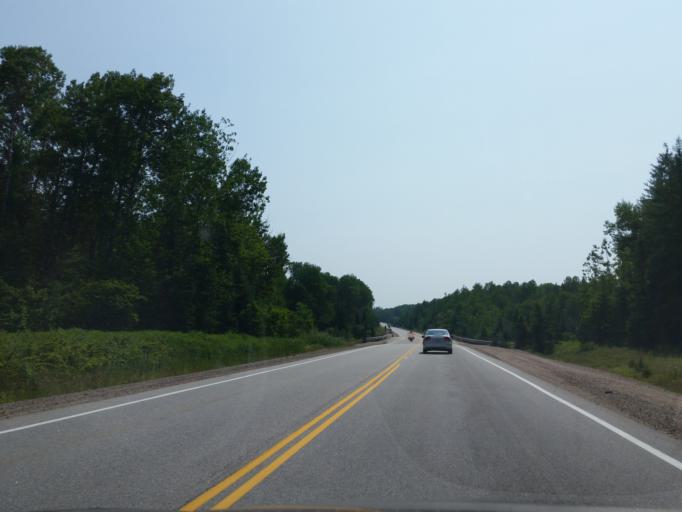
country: CA
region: Ontario
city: Mattawa
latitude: 46.2768
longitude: -78.4801
